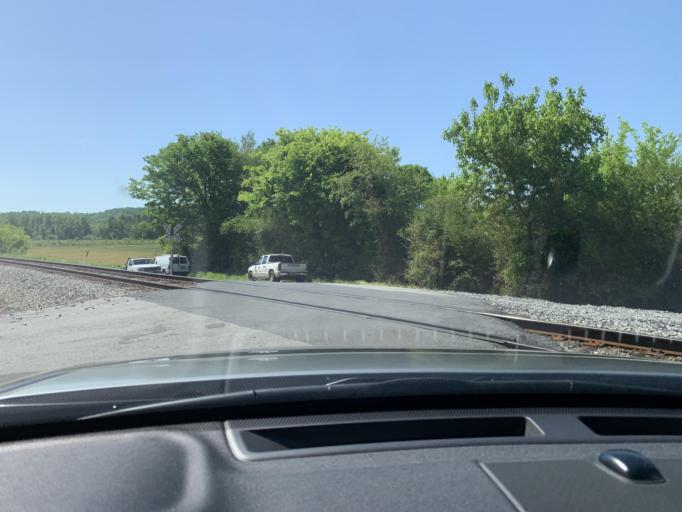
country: US
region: Georgia
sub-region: Polk County
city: Cedartown
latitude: 33.9370
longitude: -85.2098
